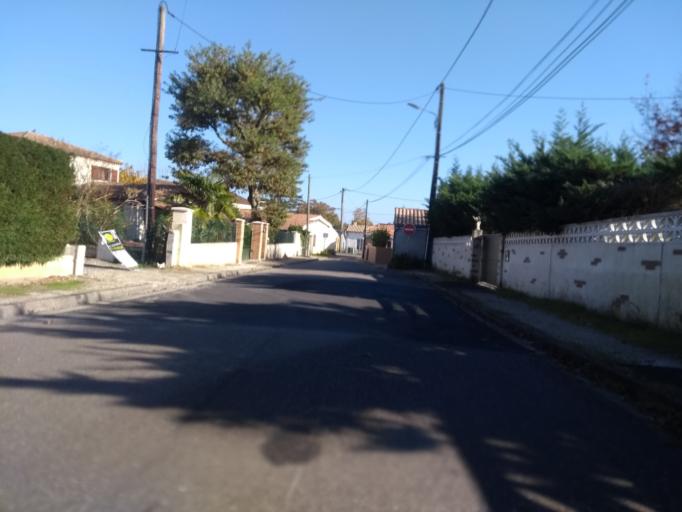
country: FR
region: Aquitaine
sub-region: Departement de la Gironde
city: Leognan
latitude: 44.7405
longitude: -0.6009
